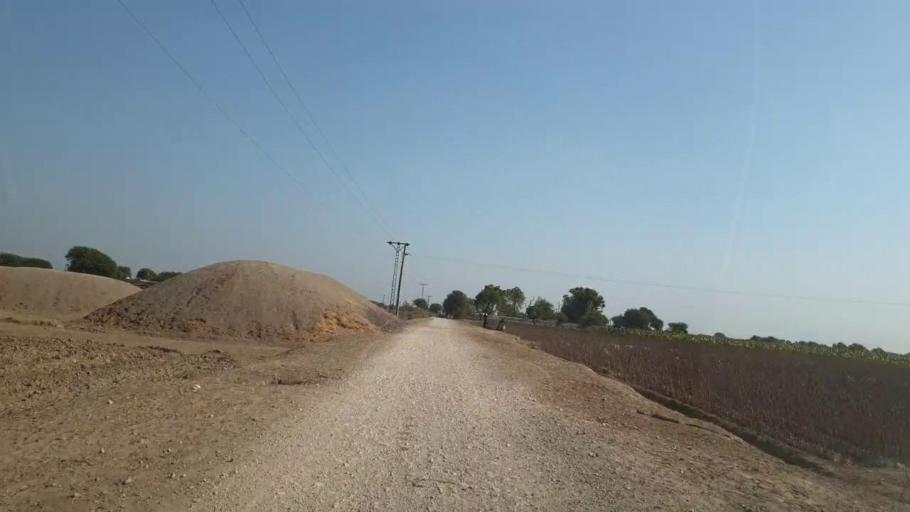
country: PK
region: Sindh
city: Tando Jam
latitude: 25.5056
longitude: 68.4938
